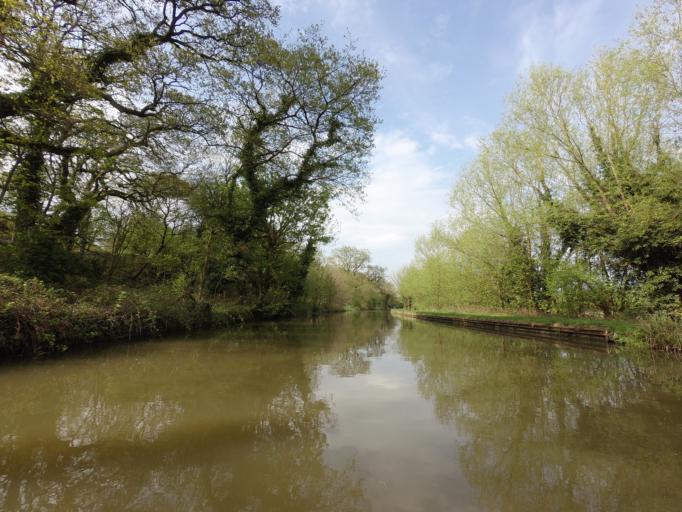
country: GB
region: England
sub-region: Central Bedfordshire
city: Leighton Buzzard
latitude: 51.9287
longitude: -0.6776
